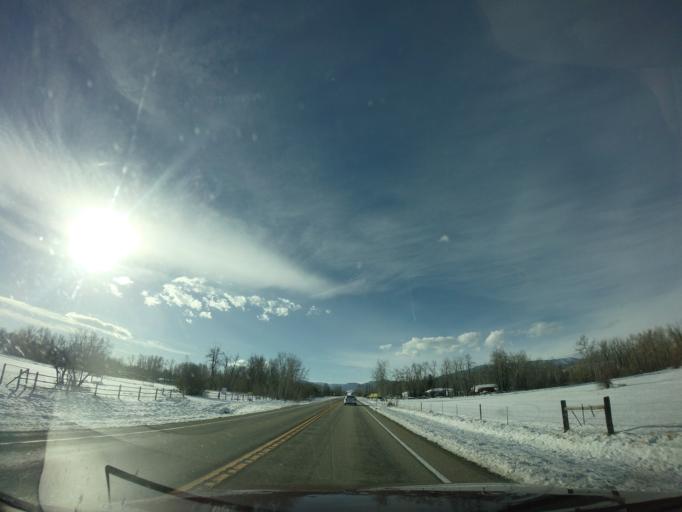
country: US
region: Montana
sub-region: Carbon County
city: Red Lodge
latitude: 45.2626
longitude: -109.2261
